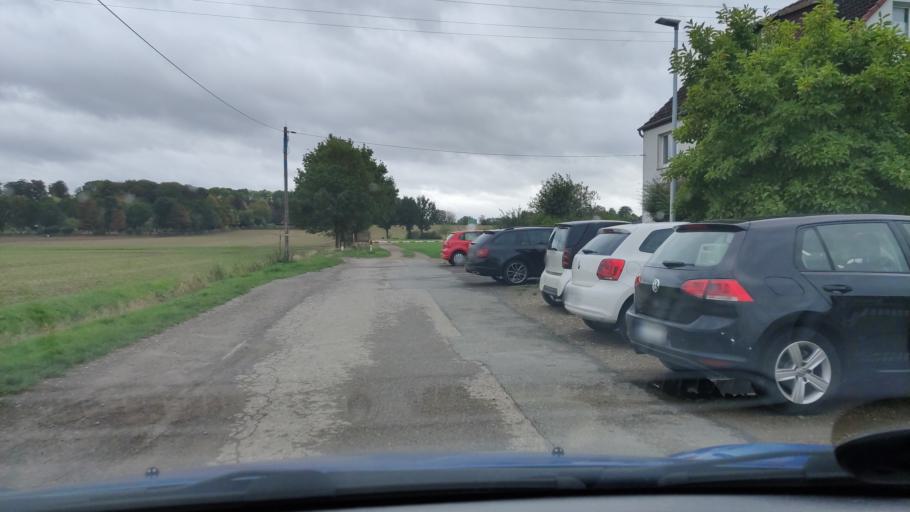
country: DE
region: Lower Saxony
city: Seelze
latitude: 52.3887
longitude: 9.6501
